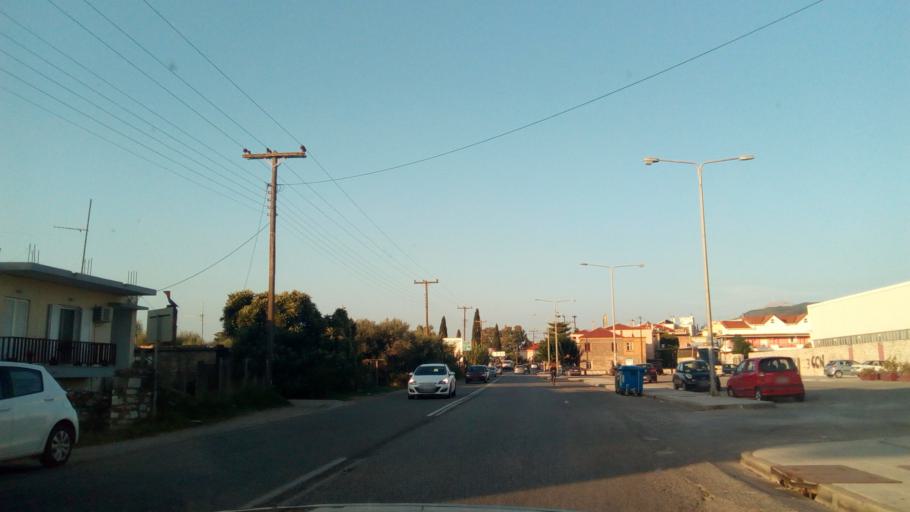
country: GR
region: West Greece
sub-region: Nomos Aitolias kai Akarnanias
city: Nafpaktos
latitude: 38.3886
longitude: 21.8163
